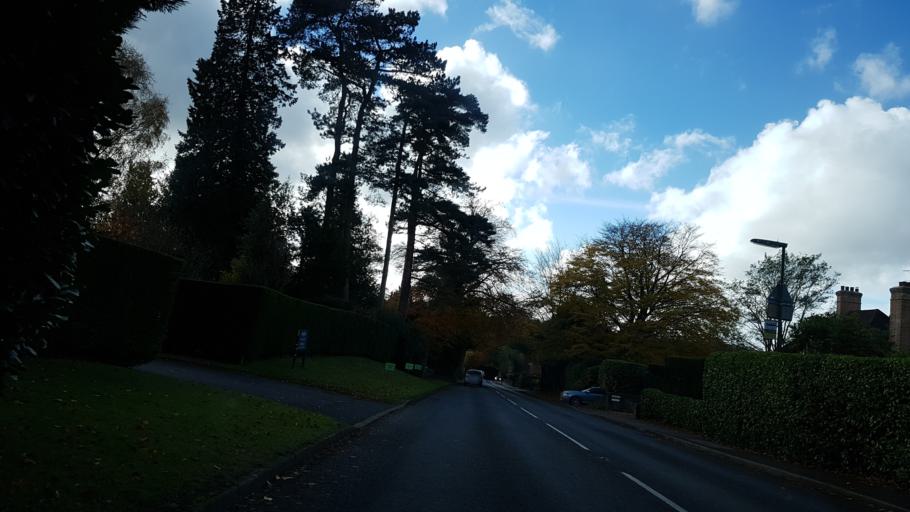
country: GB
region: England
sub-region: Surrey
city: Haslemere
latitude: 51.0930
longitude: -0.7049
